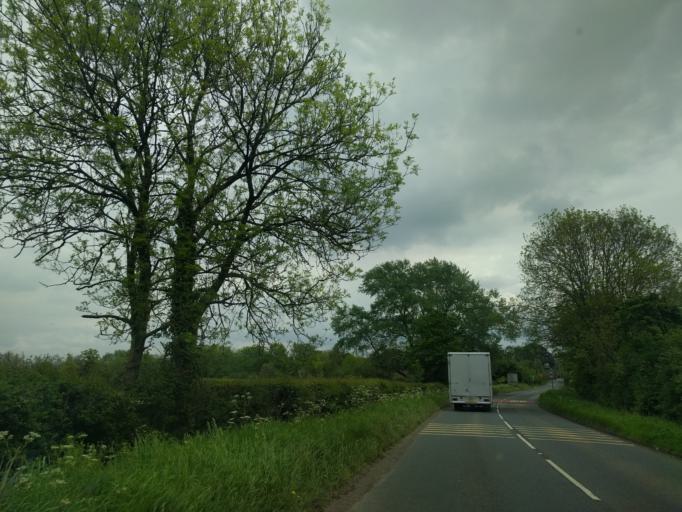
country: GB
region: England
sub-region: Somerset
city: Ilchester
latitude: 51.0763
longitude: -2.6254
